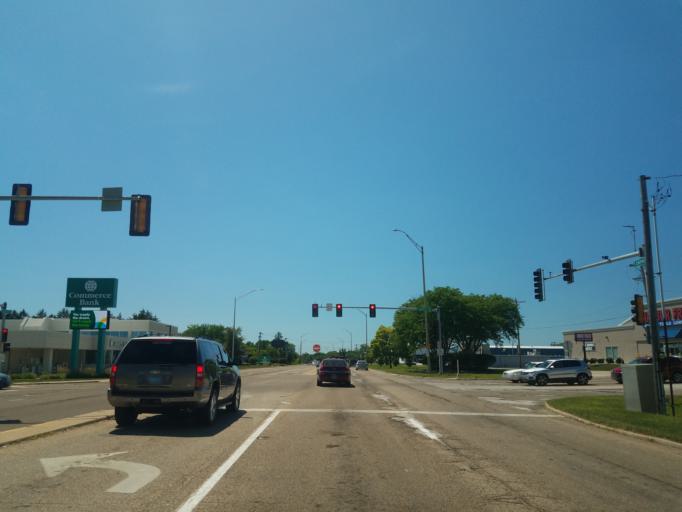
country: US
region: Illinois
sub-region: McLean County
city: Bloomington
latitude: 40.4883
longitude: -88.9607
